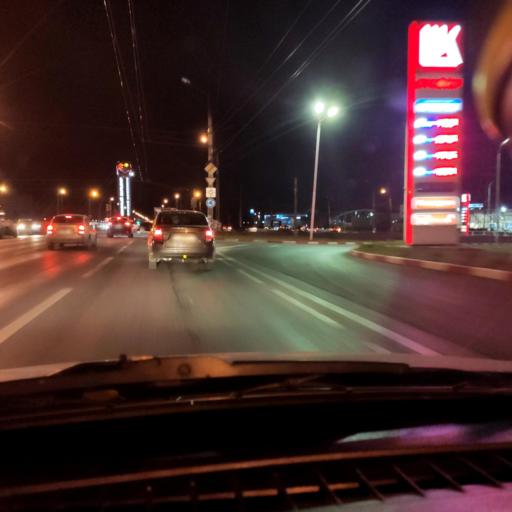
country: RU
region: Samara
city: Tol'yatti
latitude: 53.5506
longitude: 49.3198
